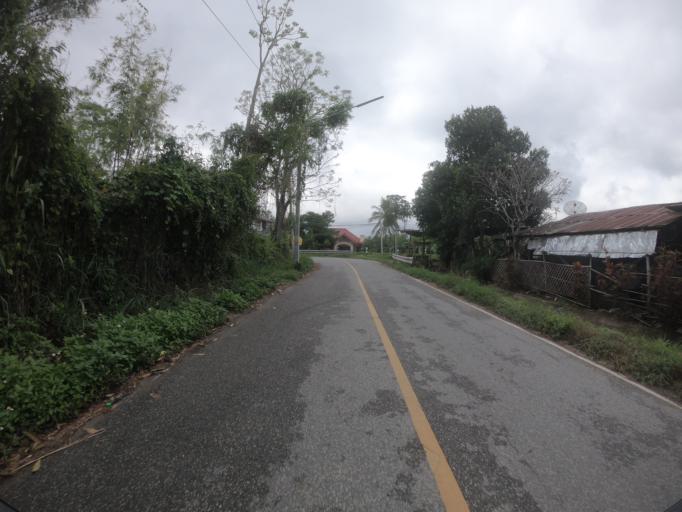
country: TH
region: Chiang Mai
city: Hang Dong
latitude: 18.7114
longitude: 98.9406
